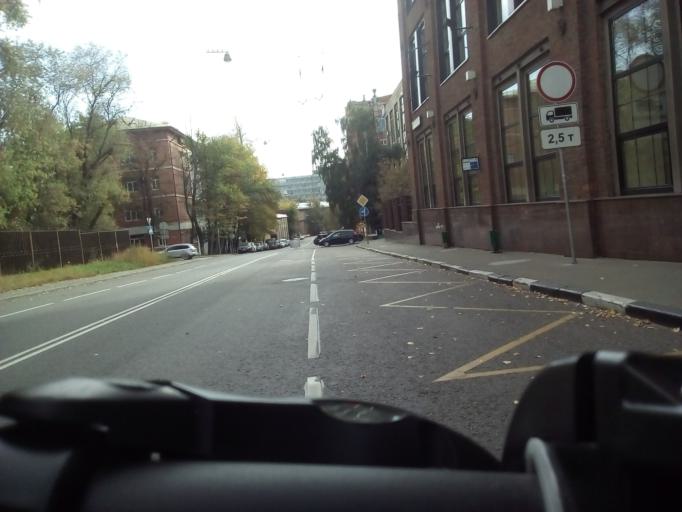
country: RU
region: Moscow
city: Lefortovo
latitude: 55.7900
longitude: 37.7071
